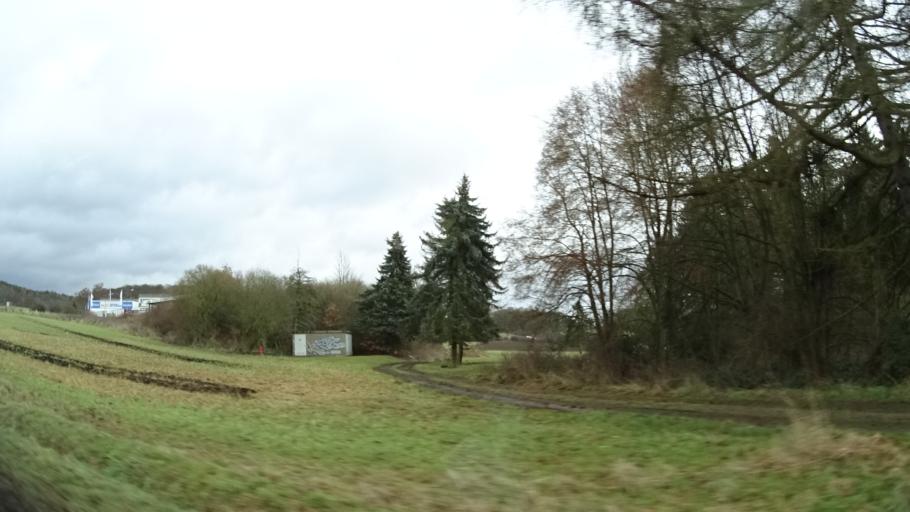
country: DE
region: Hesse
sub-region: Regierungsbezirk Giessen
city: Lauterbach
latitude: 50.6467
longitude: 9.4109
